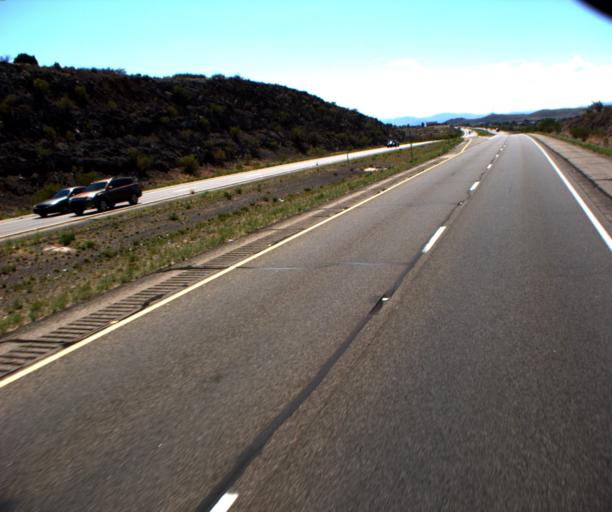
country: US
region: Arizona
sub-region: Yavapai County
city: Spring Valley
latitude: 34.3656
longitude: -112.1775
